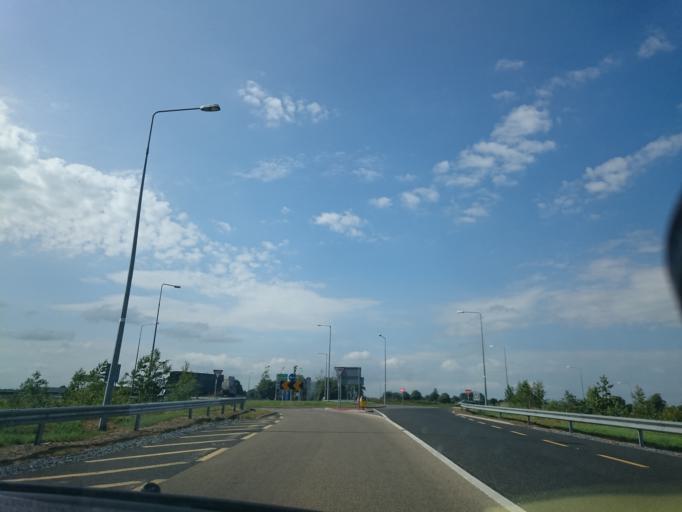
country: IE
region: Leinster
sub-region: Kilkenny
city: Kilkenny
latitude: 52.5720
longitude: -7.2313
